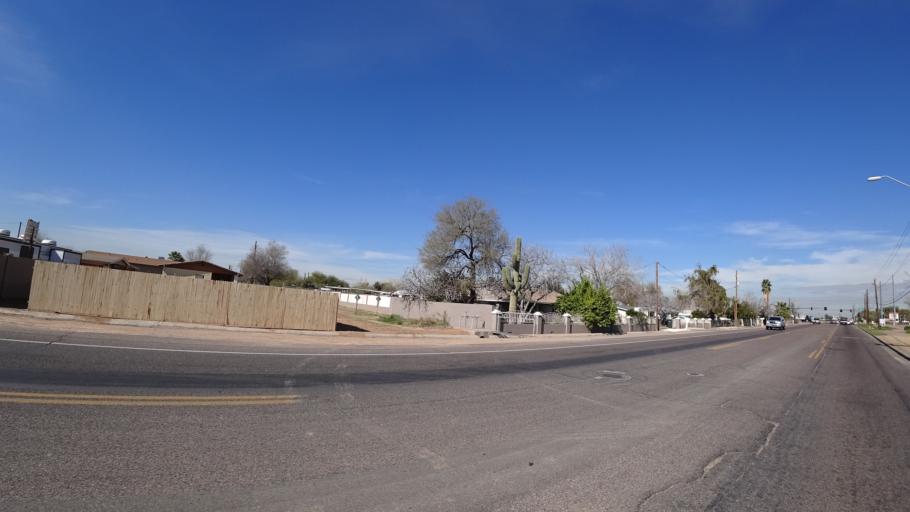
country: US
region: Arizona
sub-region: Maricopa County
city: Tolleson
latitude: 33.4209
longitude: -112.2039
